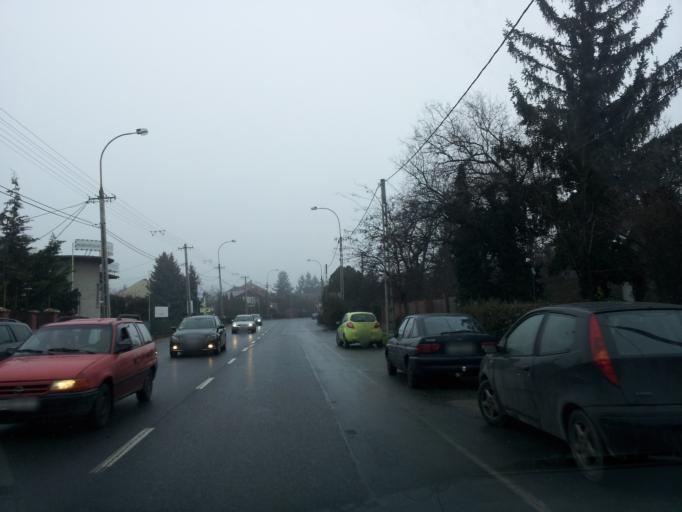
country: HU
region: Pest
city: Erd
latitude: 47.3892
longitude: 18.9340
